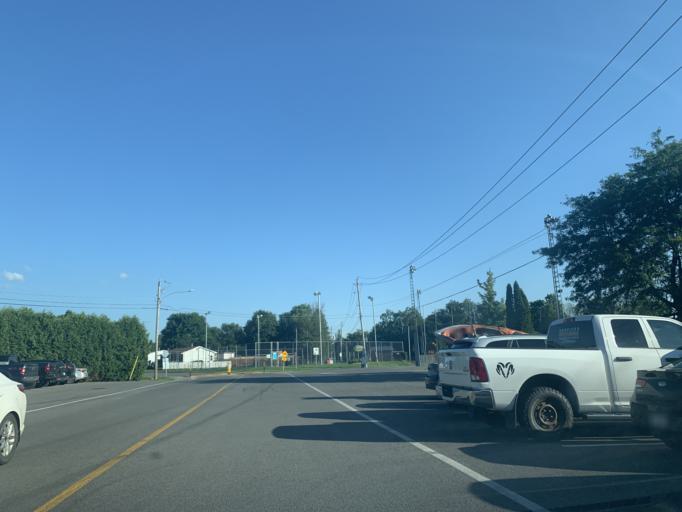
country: CA
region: Ontario
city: Hawkesbury
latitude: 45.6297
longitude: -74.6007
